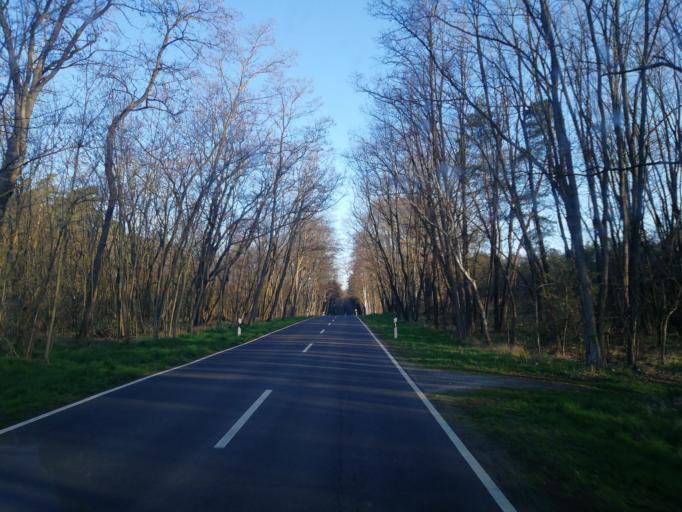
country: DE
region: Brandenburg
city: Drahnsdorf
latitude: 51.8985
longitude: 13.6064
